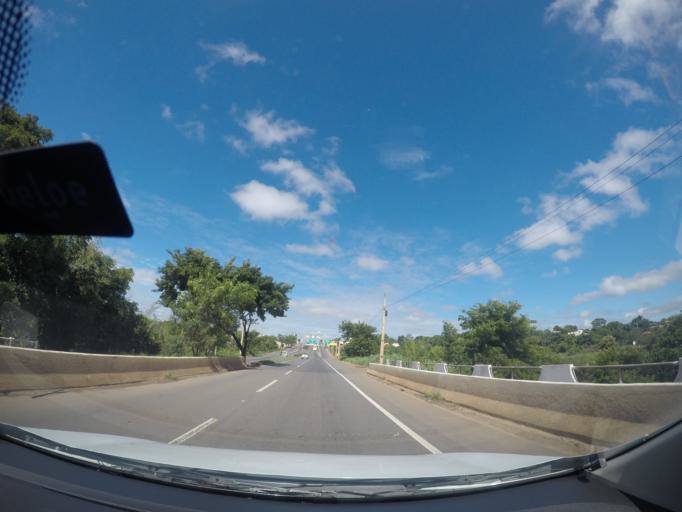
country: BR
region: Goias
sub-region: Goiania
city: Goiania
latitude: -16.6220
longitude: -49.2398
